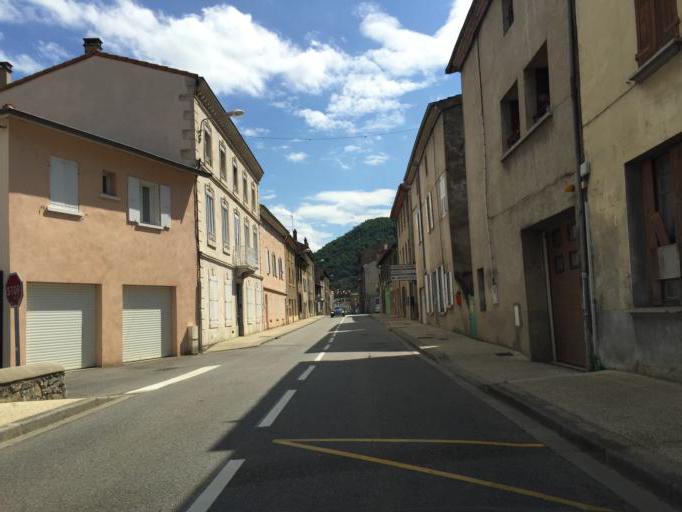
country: FR
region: Rhone-Alpes
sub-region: Departement de l'Ardeche
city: Andance
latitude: 45.2434
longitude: 4.8000
